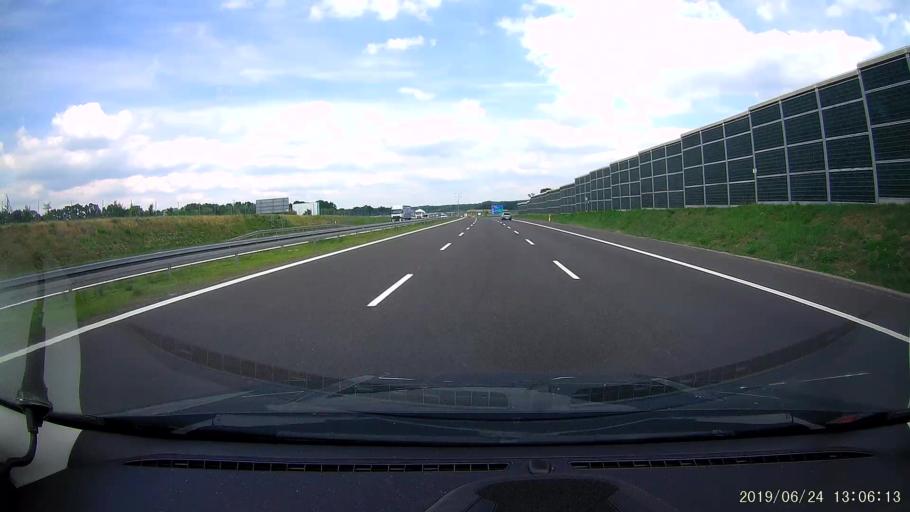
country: PL
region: Silesian Voivodeship
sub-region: Powiat rybnicki
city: Stanowice
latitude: 50.1238
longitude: 18.6881
